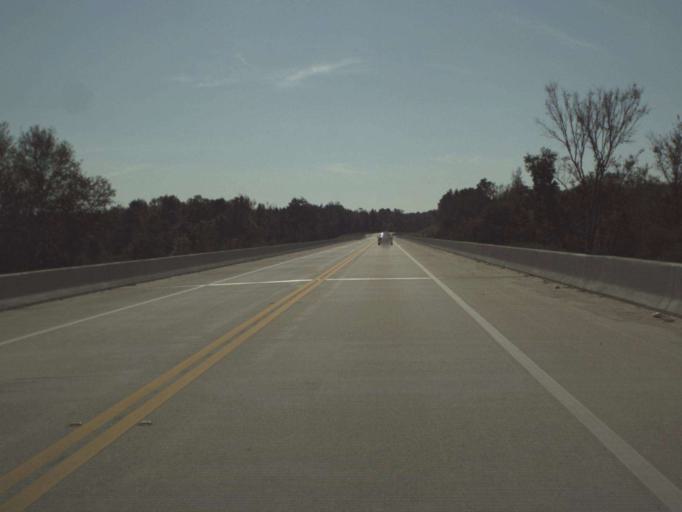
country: US
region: Florida
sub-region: Gadsden County
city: Quincy
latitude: 30.5858
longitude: -84.5515
